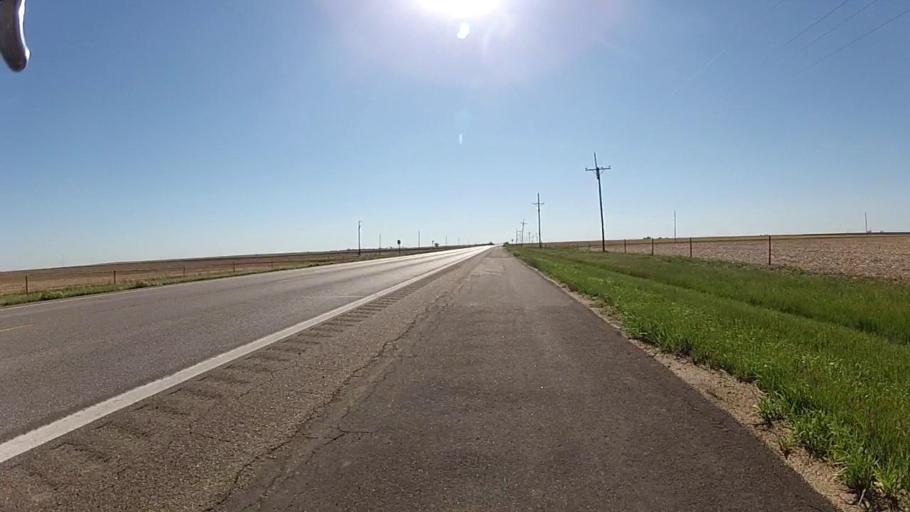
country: US
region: Kansas
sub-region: Kiowa County
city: Greensburg
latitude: 37.5863
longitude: -99.6685
